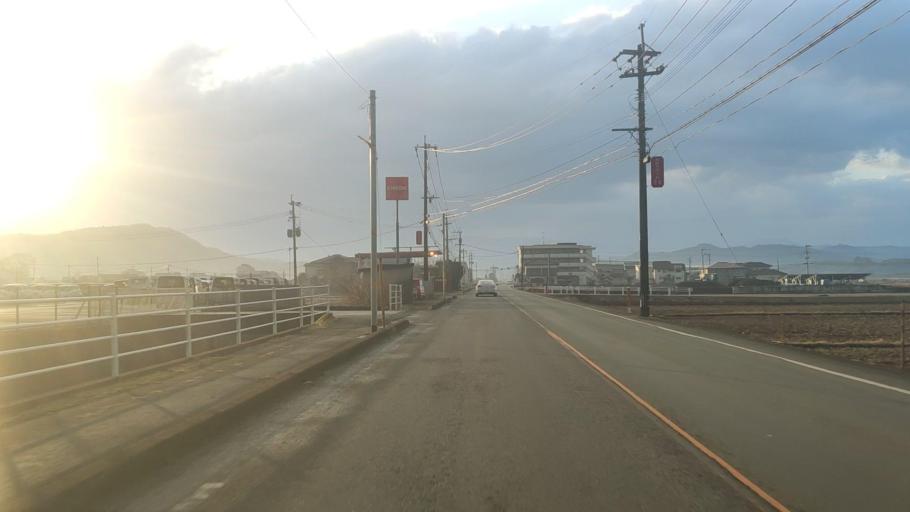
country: JP
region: Kumamoto
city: Uto
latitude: 32.7148
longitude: 130.7733
